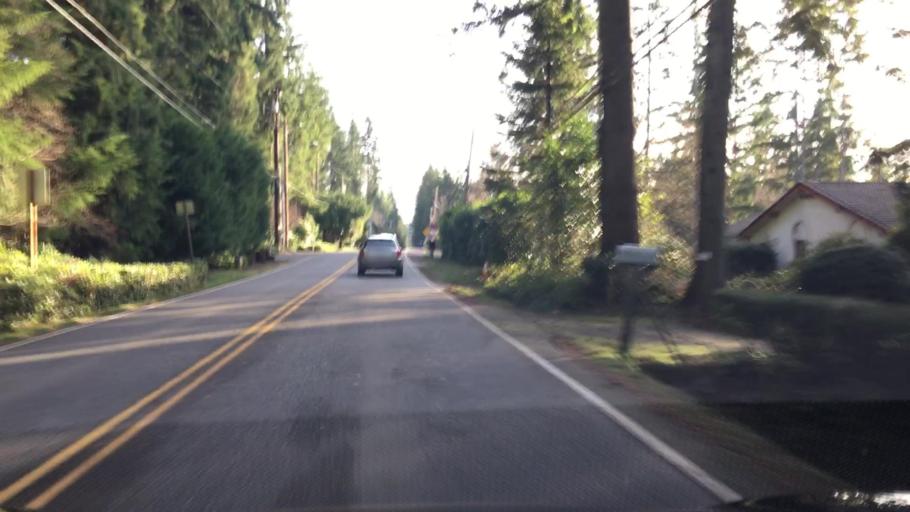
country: US
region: Washington
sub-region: Snohomish County
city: Maltby
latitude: 47.7767
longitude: -122.1319
